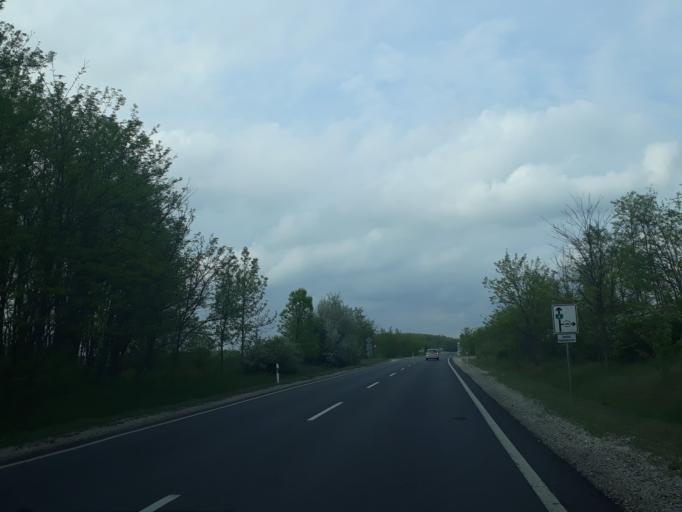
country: HU
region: Szabolcs-Szatmar-Bereg
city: Nyirtass
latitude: 48.1039
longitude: 21.9879
